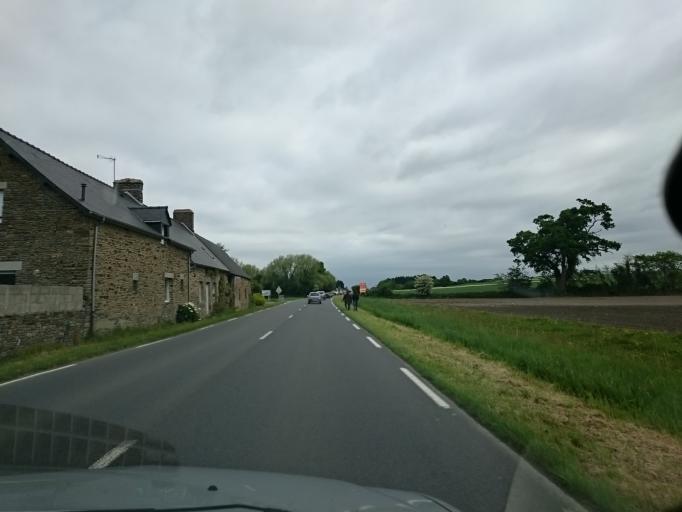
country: FR
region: Lower Normandy
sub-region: Departement de la Manche
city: Pontorson
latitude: 48.5765
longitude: -1.5124
